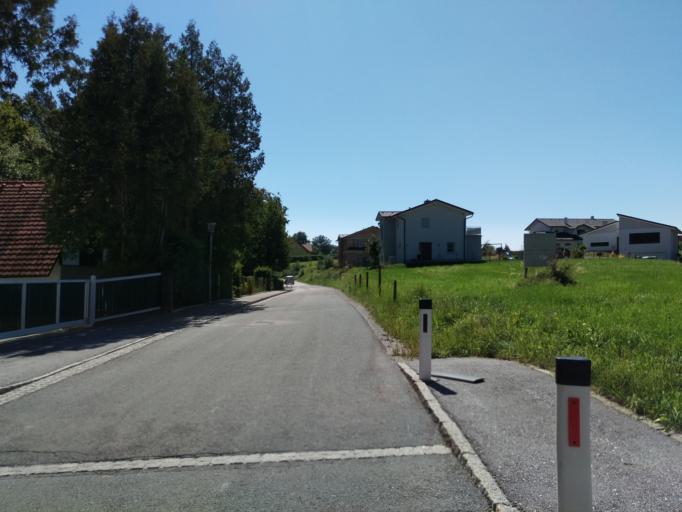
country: AT
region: Styria
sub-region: Politischer Bezirk Graz-Umgebung
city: Eggersdorf bei Graz
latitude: 47.0885
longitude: 15.5605
